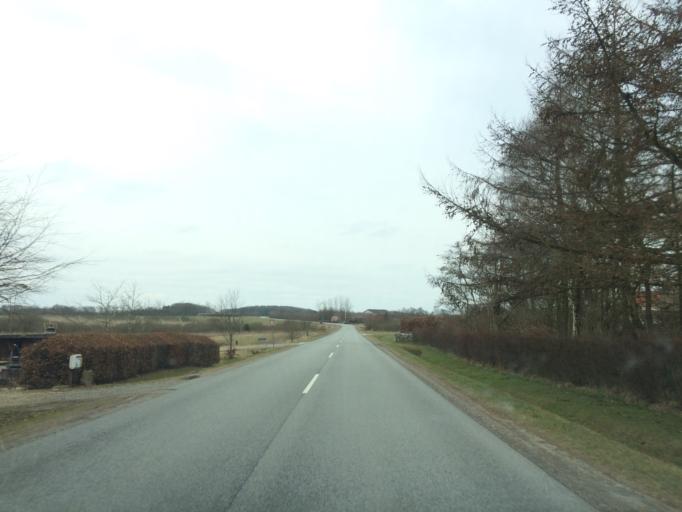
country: DK
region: Central Jutland
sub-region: Ringkobing-Skjern Kommune
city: Tarm
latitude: 55.8284
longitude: 8.4306
